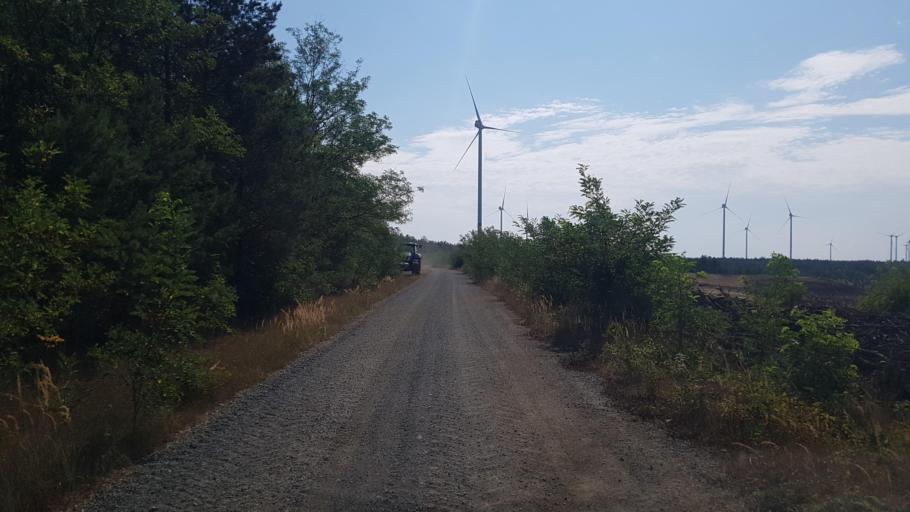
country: DE
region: Brandenburg
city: Schipkau
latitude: 51.5436
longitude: 13.8580
